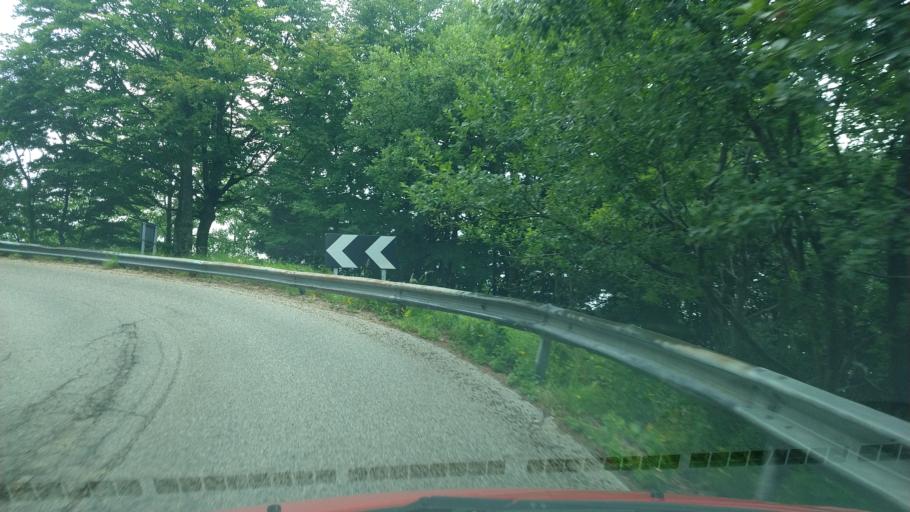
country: IT
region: Veneto
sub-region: Provincia di Vicenza
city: Longhi
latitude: 45.8811
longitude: 11.3201
